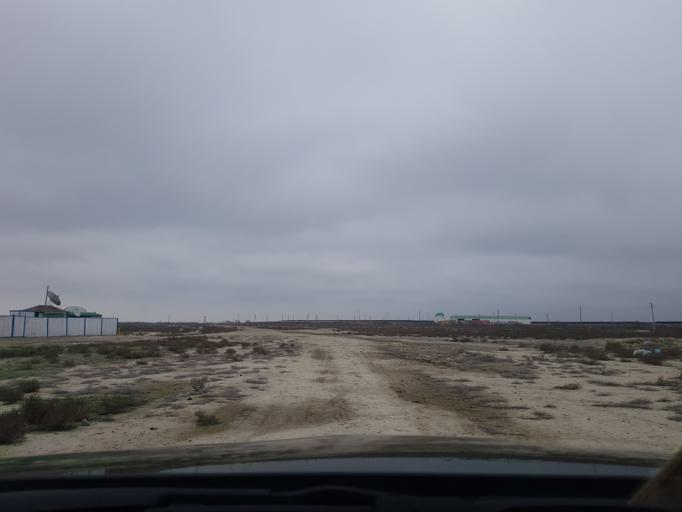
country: TM
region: Ahal
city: Abadan
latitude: 38.1395
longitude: 57.9732
